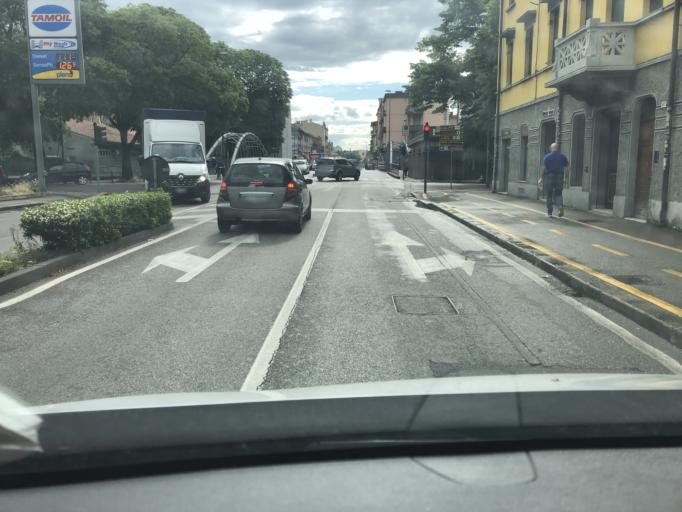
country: IT
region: Veneto
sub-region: Provincia di Verona
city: Verona
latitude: 45.4436
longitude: 10.9694
